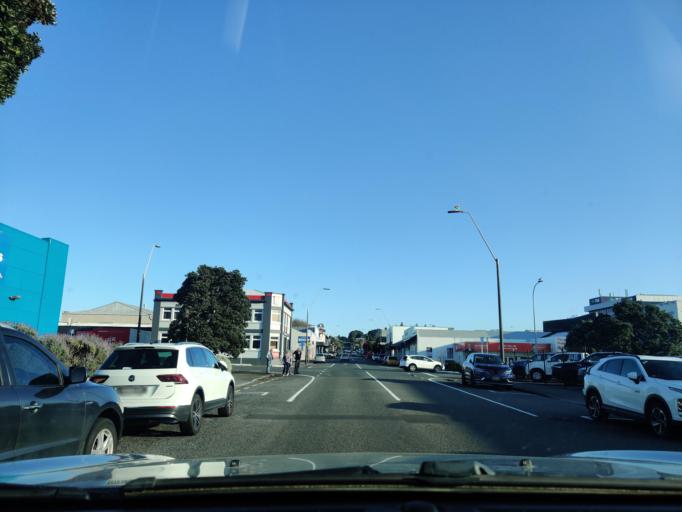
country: NZ
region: Taranaki
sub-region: New Plymouth District
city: New Plymouth
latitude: -39.0550
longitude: 174.0784
